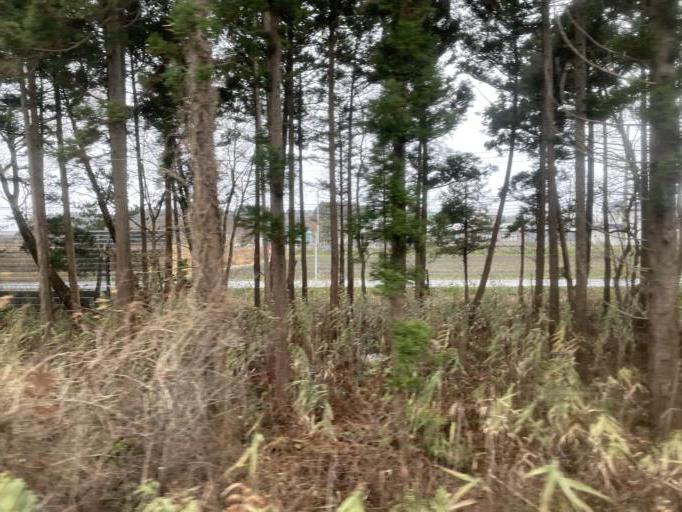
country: JP
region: Aomori
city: Aomori Shi
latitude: 40.9854
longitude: 140.6530
